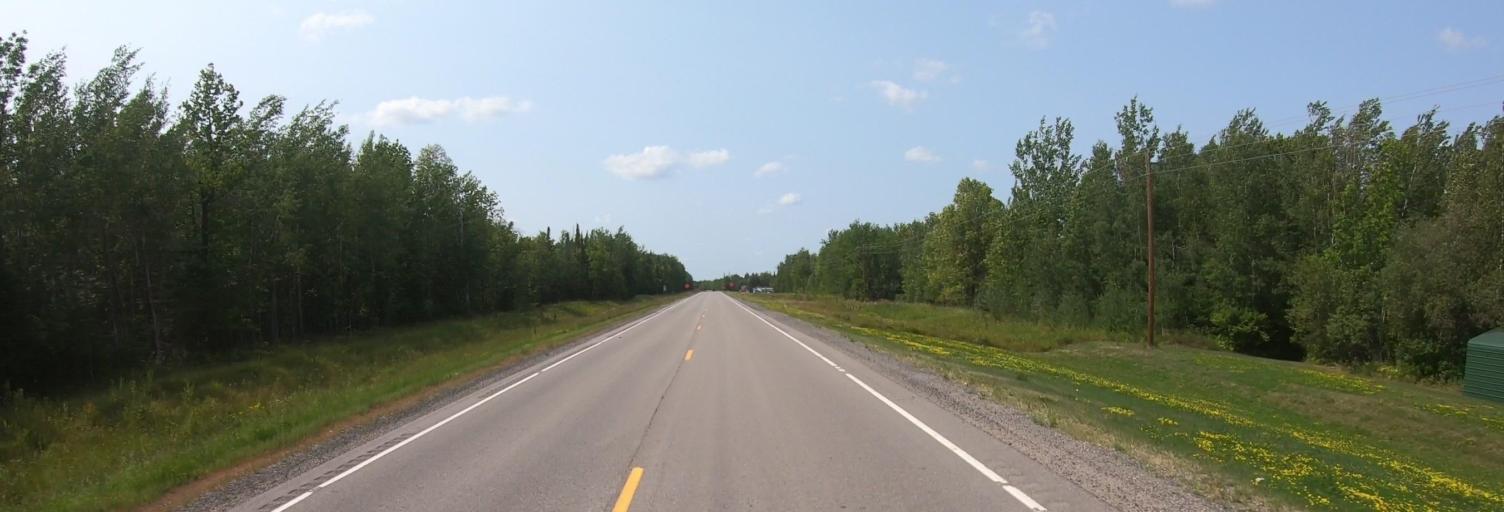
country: US
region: Minnesota
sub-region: Lake of the Woods County
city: Baudette
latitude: 48.6946
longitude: -94.4750
